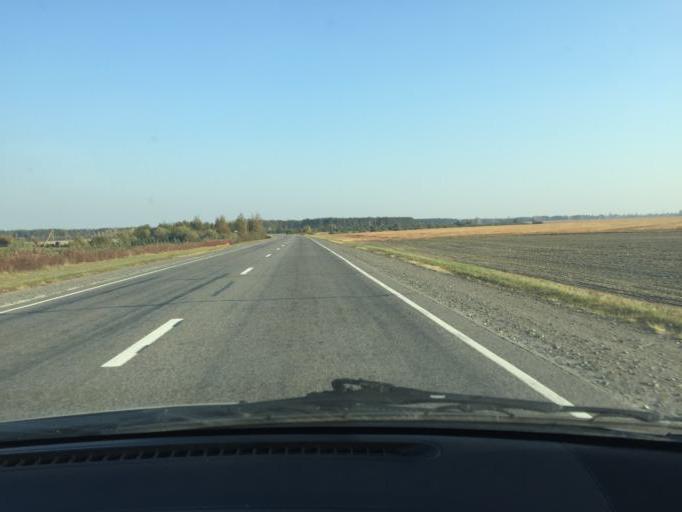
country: BY
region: Brest
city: Davyd-Haradok
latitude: 52.2510
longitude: 27.0639
